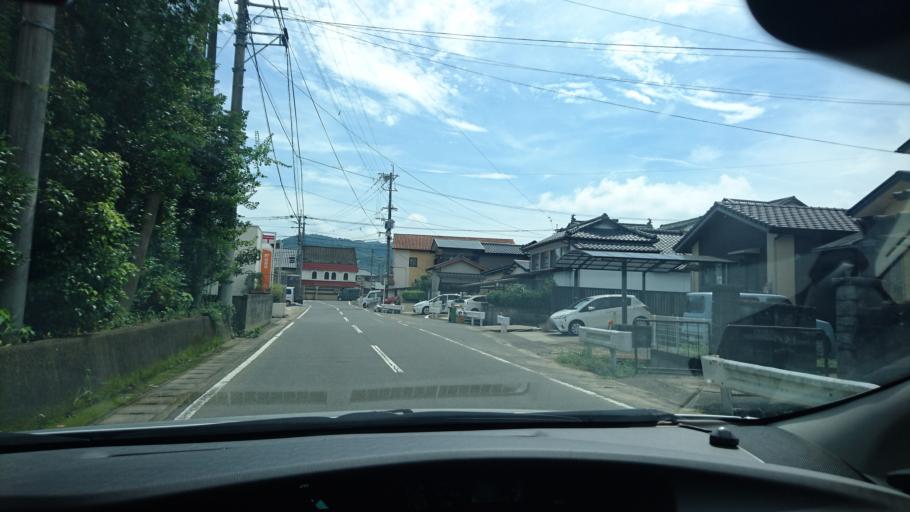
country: JP
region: Saga Prefecture
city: Takeocho-takeo
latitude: 33.2213
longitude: 130.0721
